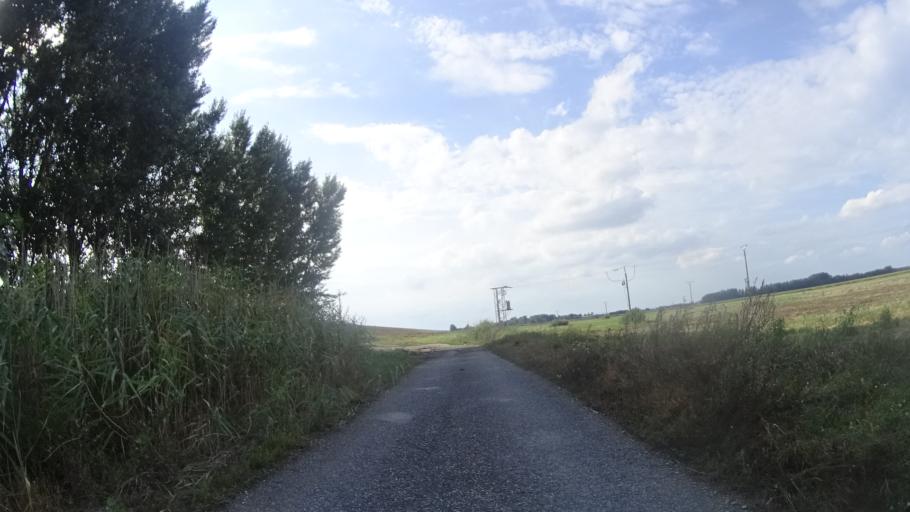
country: HU
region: Gyor-Moson-Sopron
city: Asvanyraro
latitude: 47.9297
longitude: 17.4737
